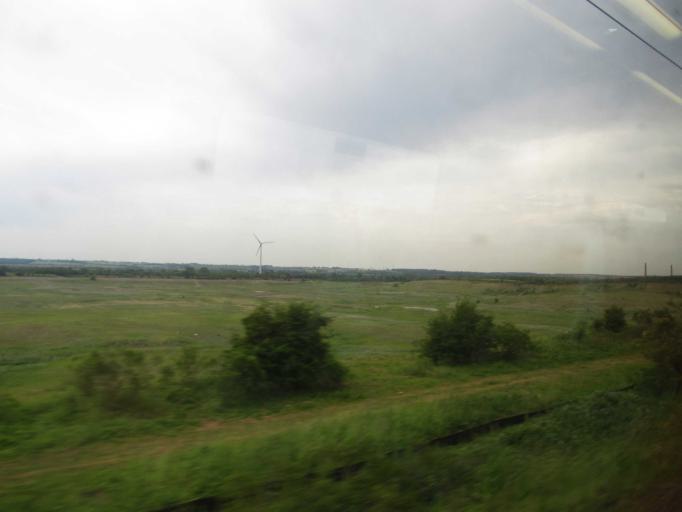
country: GB
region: England
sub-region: Bedford
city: Stewartby
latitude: 52.0530
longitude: -0.5139
